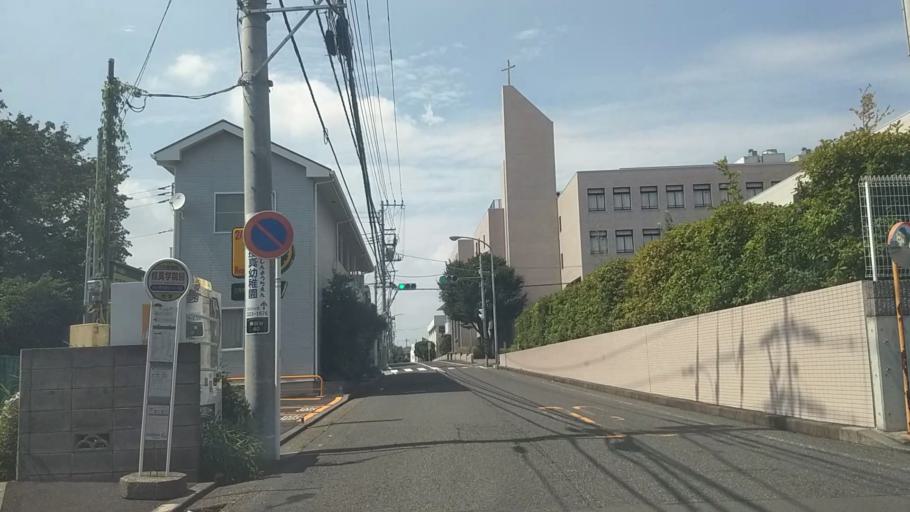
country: JP
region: Kanagawa
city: Yokohama
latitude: 35.4802
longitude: 139.6207
